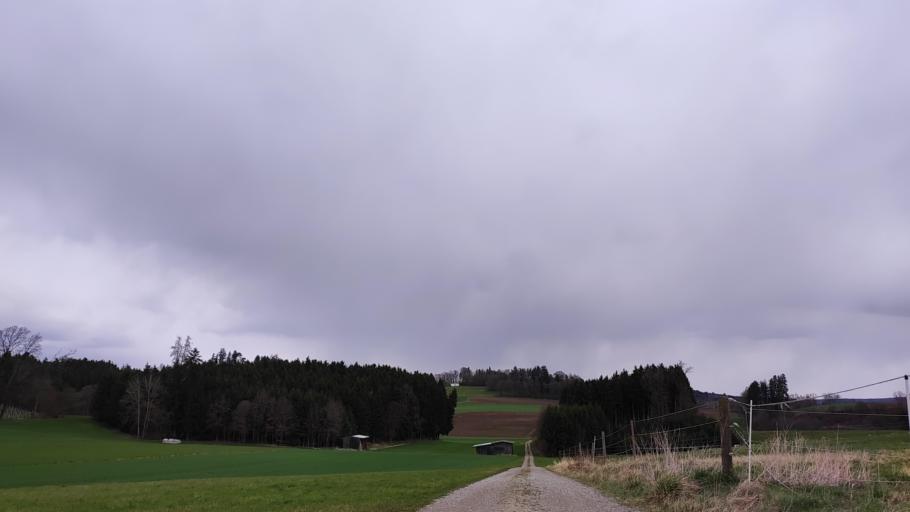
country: DE
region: Bavaria
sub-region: Swabia
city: Dinkelscherben
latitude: 48.3691
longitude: 10.5600
